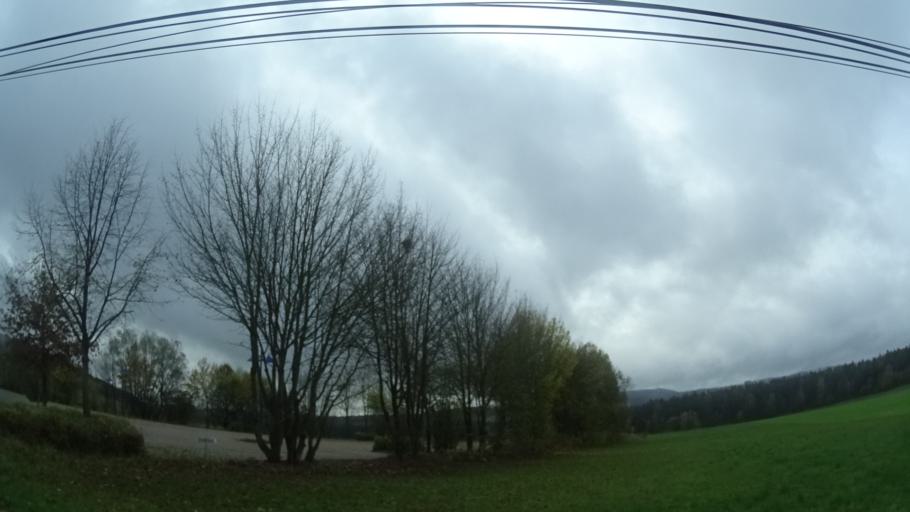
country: DE
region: Thuringia
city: Eisfeld
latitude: 50.4878
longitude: 10.8444
